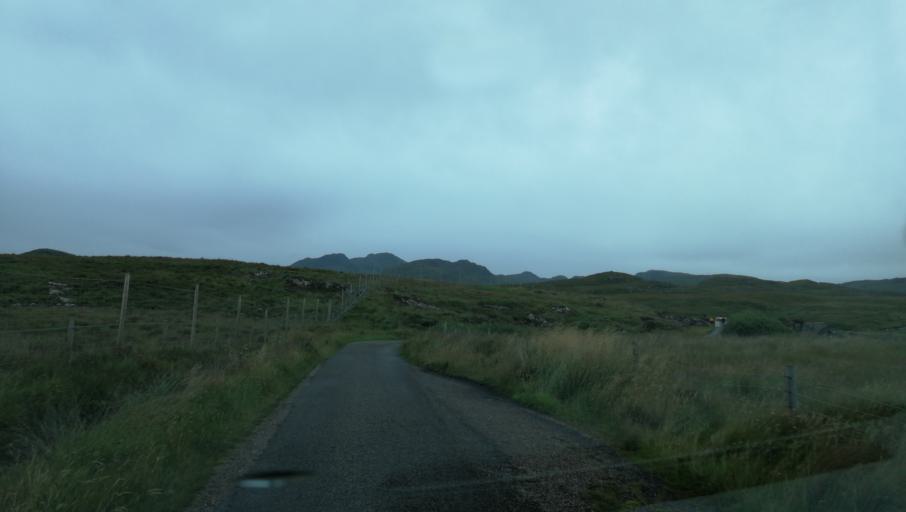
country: GB
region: Scotland
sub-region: Argyll and Bute
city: Isle Of Mull
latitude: 56.7231
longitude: -6.2202
